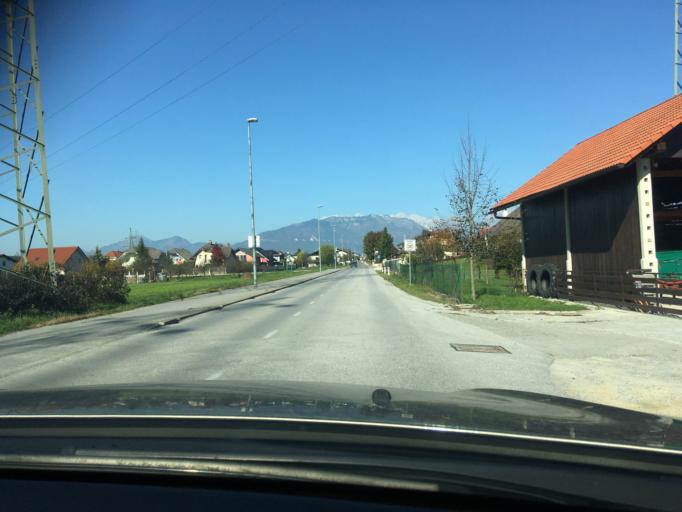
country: SI
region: Domzale
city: Vir
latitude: 46.1433
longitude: 14.6090
